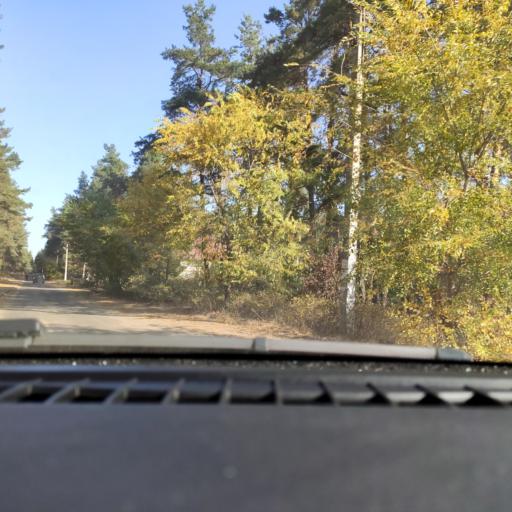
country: RU
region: Voronezj
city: Maslovka
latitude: 51.5466
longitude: 39.2213
